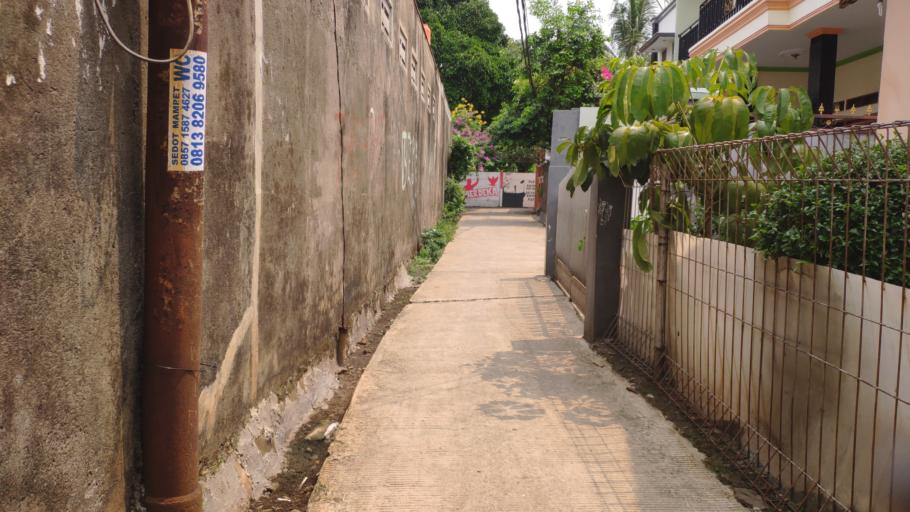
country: ID
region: West Java
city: Depok
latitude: -6.3709
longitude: 106.8078
